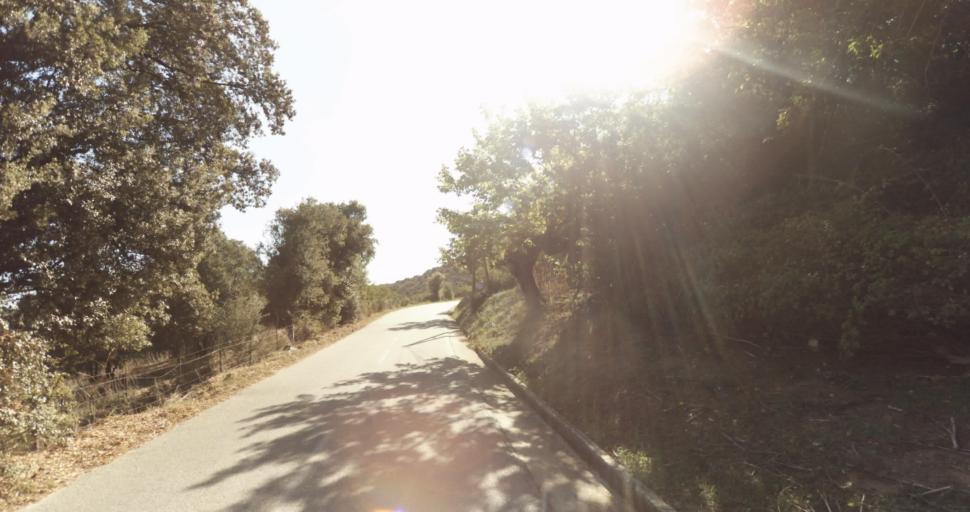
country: FR
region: Corsica
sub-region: Departement de la Corse-du-Sud
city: Ajaccio
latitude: 41.9295
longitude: 8.7027
